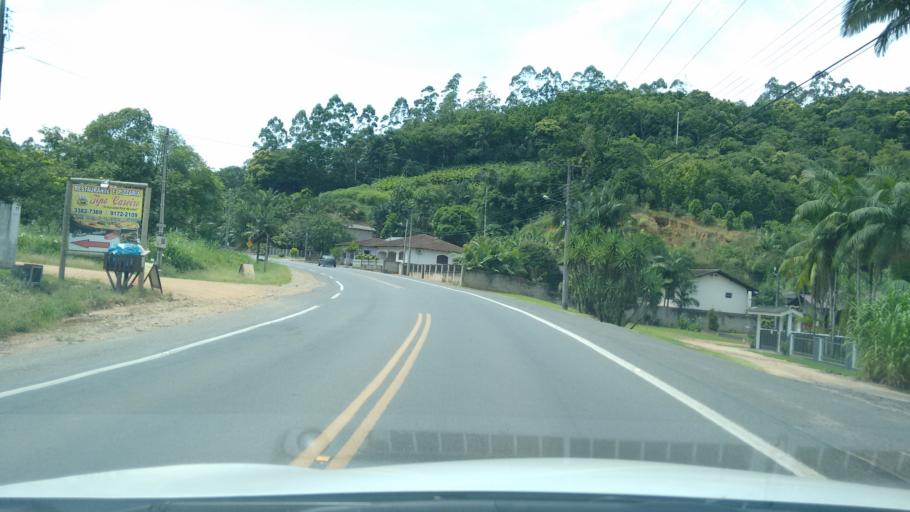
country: BR
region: Santa Catarina
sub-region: Rodeio
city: Gavea
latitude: -26.8980
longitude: -49.3534
